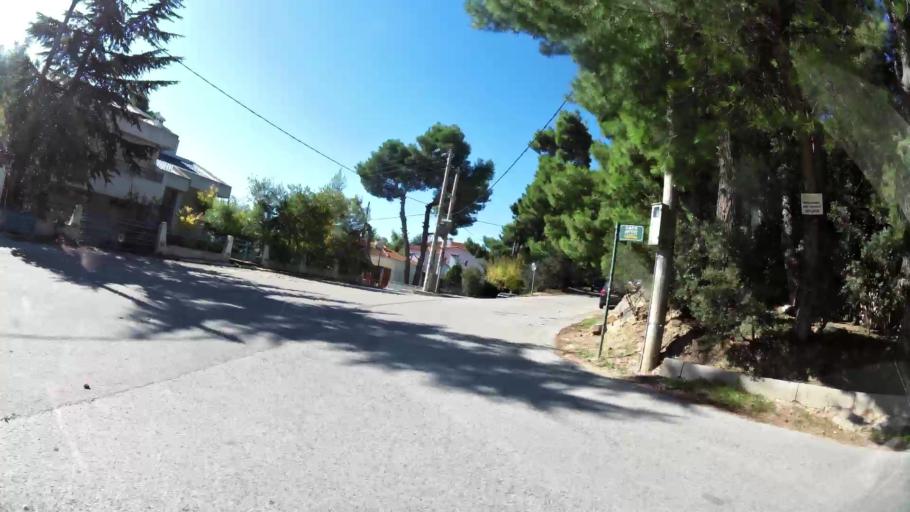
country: GR
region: Attica
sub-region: Nomarchia Anatolikis Attikis
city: Rodopoli
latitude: 38.1099
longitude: 23.8830
